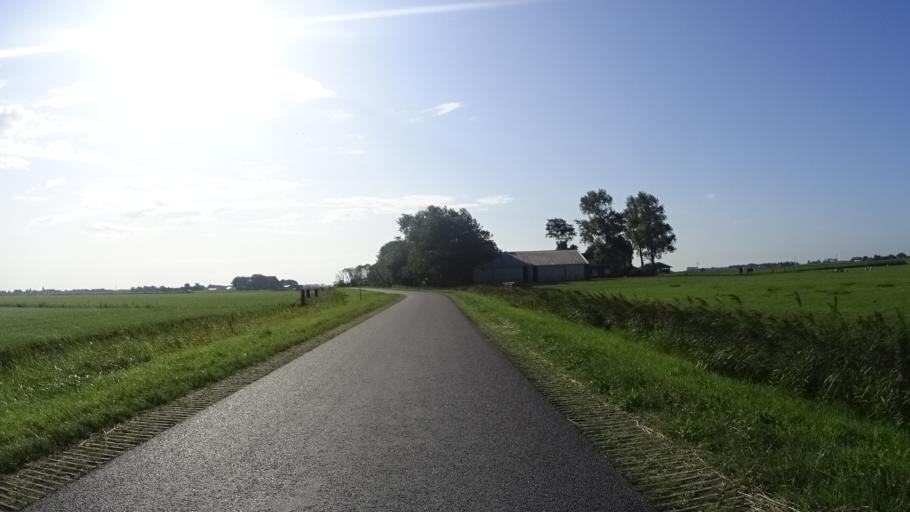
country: NL
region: Friesland
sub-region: Sudwest Fryslan
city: Makkum
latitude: 53.1140
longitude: 5.4046
